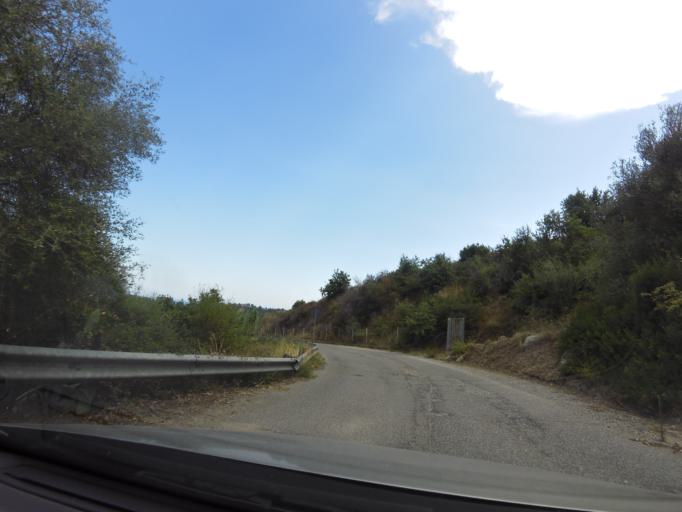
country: IT
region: Calabria
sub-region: Provincia di Reggio Calabria
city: Camini
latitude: 38.4301
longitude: 16.5136
